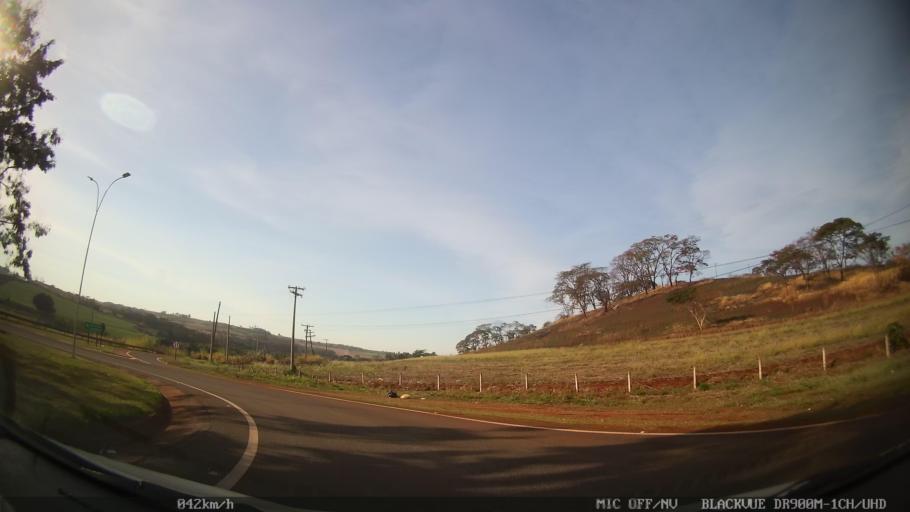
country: BR
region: Sao Paulo
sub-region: Cravinhos
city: Cravinhos
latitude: -21.2785
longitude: -47.8037
